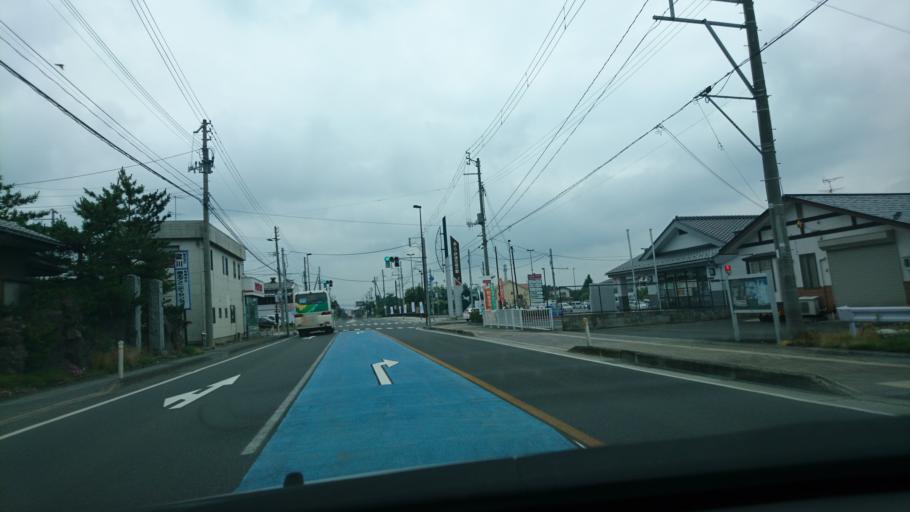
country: JP
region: Miyagi
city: Furukawa
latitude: 38.7087
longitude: 140.8336
